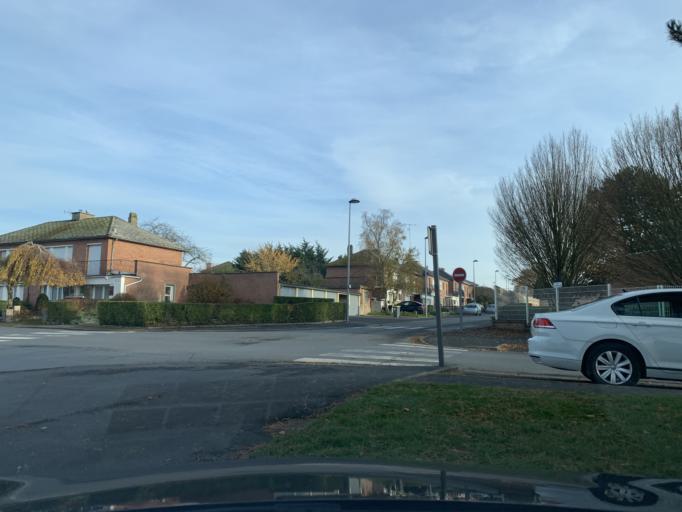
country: FR
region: Nord-Pas-de-Calais
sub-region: Departement du Nord
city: Cambrai
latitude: 50.1613
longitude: 3.2603
